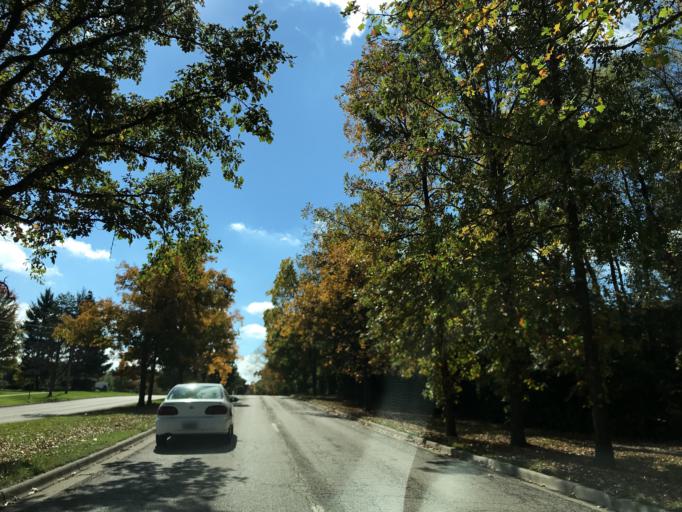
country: US
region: Michigan
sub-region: Washtenaw County
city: Ann Arbor
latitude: 42.2916
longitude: -83.6825
